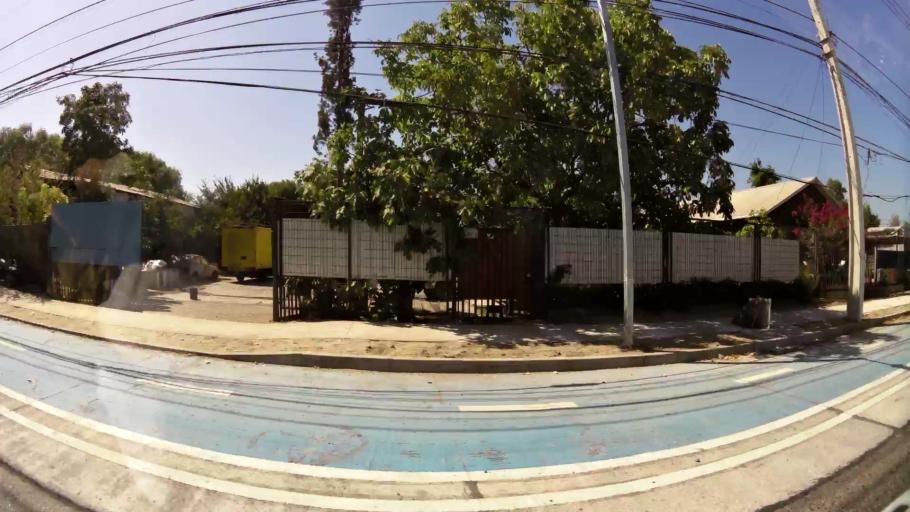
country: CL
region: Maule
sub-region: Provincia de Talca
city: Talca
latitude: -35.4259
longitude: -71.6386
